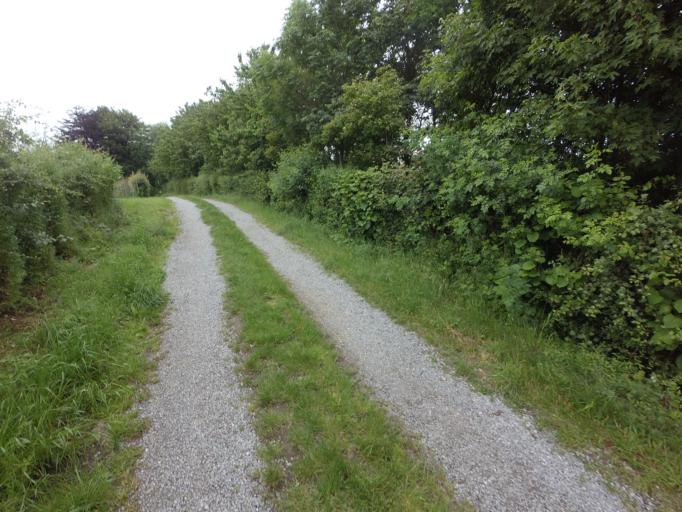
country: NL
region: Limburg
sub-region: Gemeente Voerendaal
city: Ubachsberg
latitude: 50.8437
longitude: 5.9487
